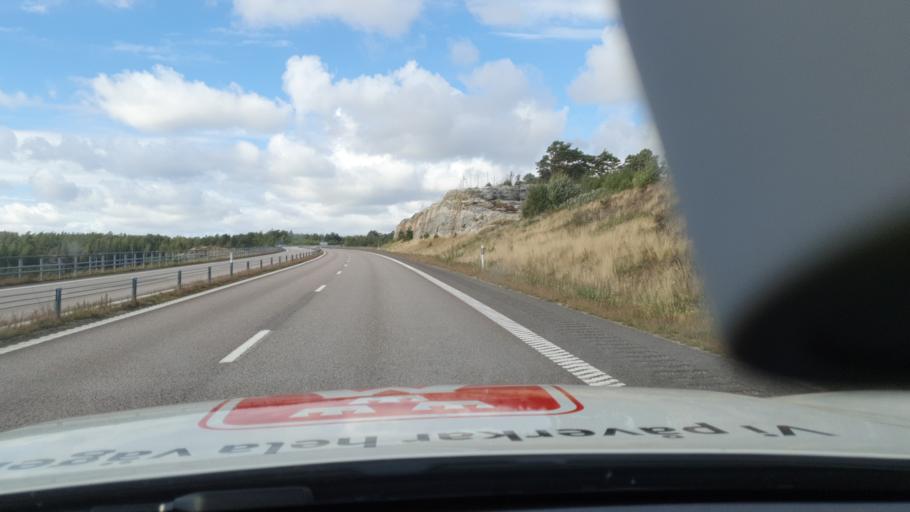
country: SE
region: Vaestra Goetaland
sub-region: Stromstads Kommun
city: Stroemstad
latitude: 58.8816
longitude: 11.2738
